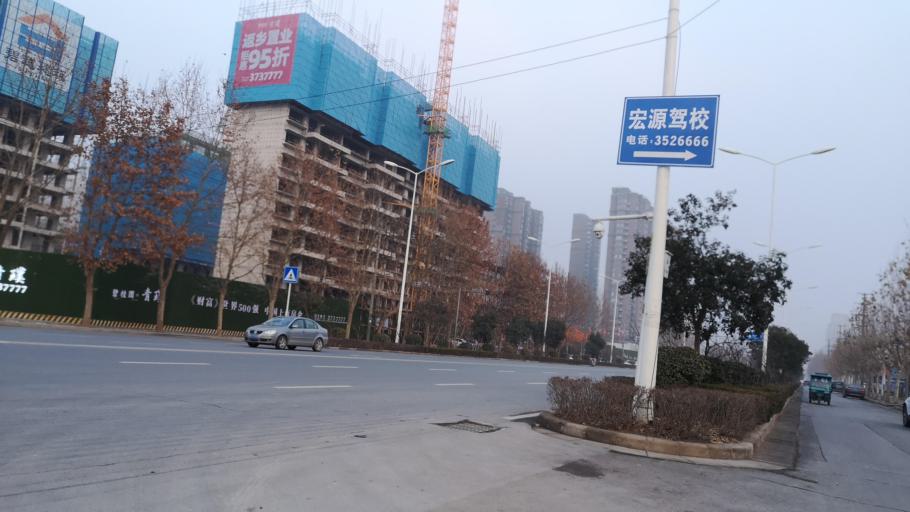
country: CN
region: Henan Sheng
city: Zhongyuanlu
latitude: 35.7476
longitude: 115.0562
